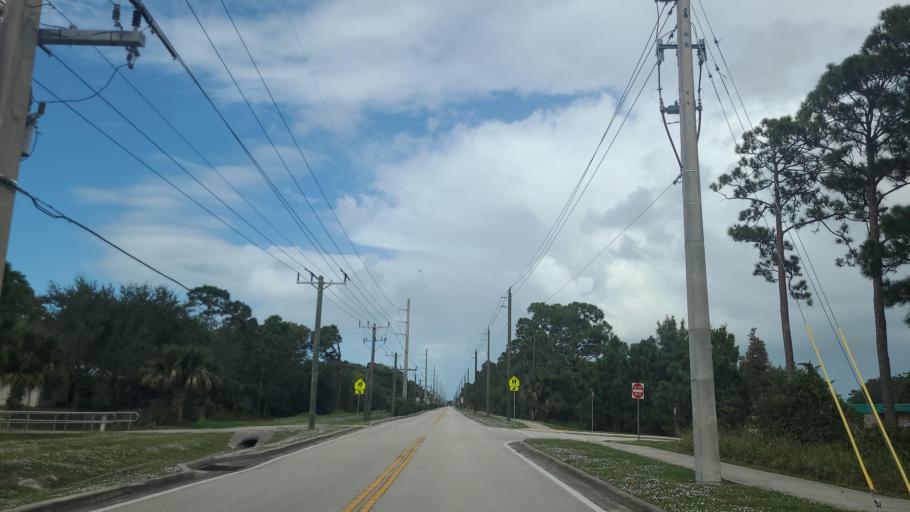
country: US
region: Florida
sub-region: Indian River County
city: Sebastian
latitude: 27.8031
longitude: -80.4782
